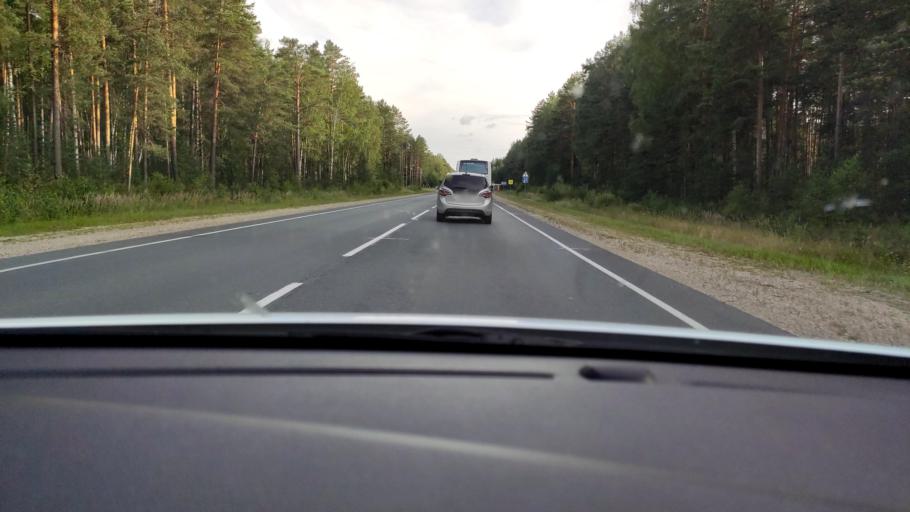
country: RU
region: Mariy-El
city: Suslonger
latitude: 56.3130
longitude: 48.2348
